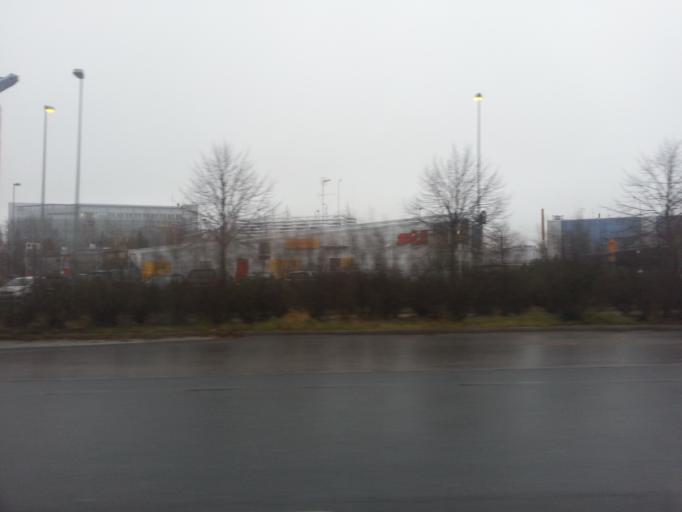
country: FI
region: Uusimaa
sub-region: Helsinki
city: Vantaa
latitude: 60.3129
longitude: 24.9700
